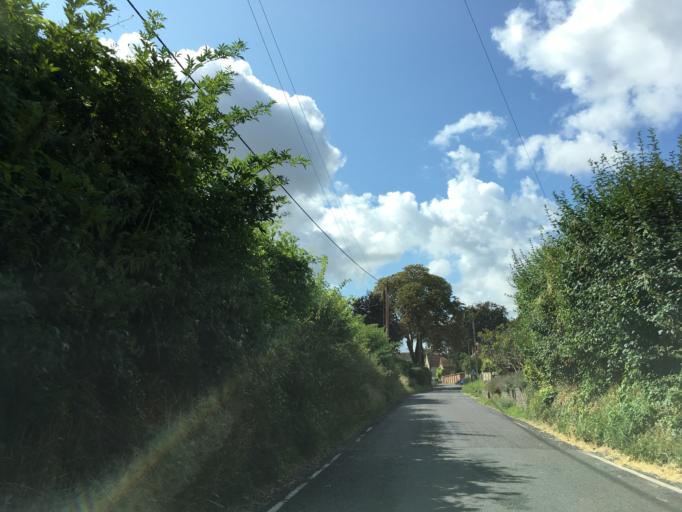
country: GB
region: England
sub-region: Hampshire
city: Kings Worthy
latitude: 51.1697
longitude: -1.3780
